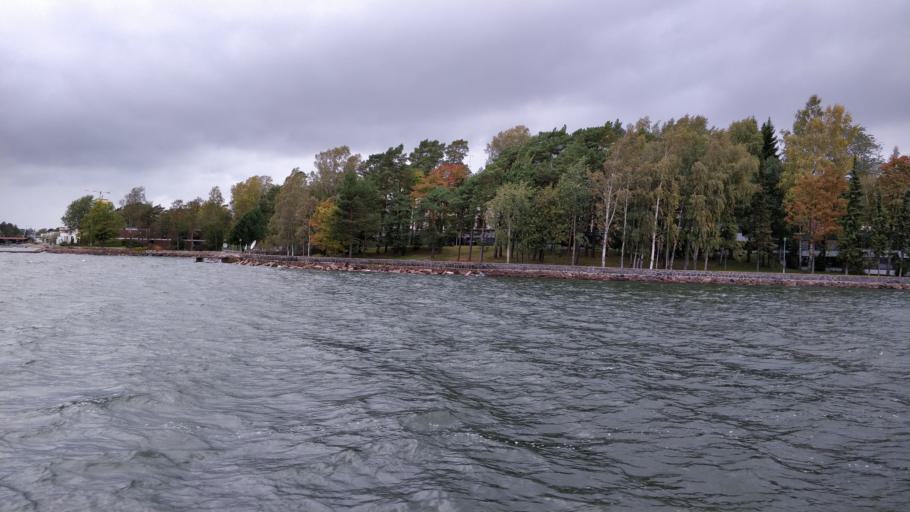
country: FI
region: Uusimaa
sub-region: Helsinki
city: Helsinki
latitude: 60.1784
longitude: 25.0172
